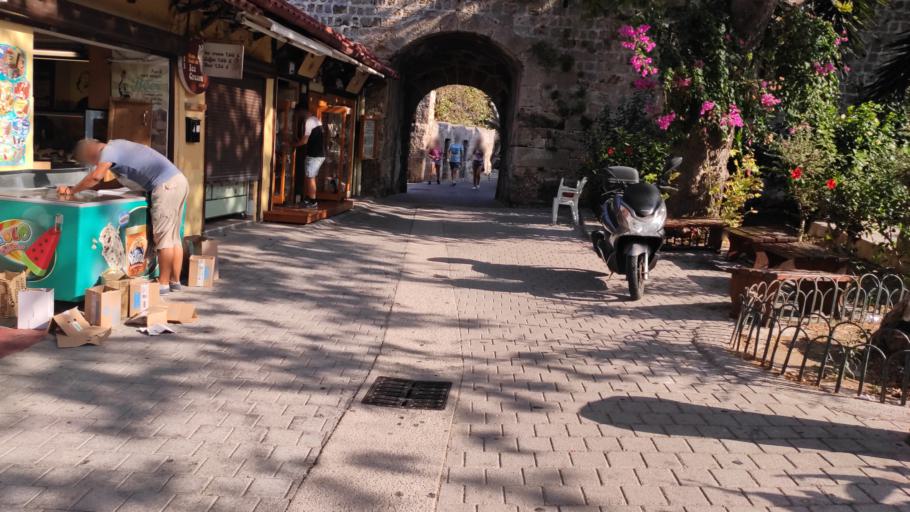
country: GR
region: South Aegean
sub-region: Nomos Dodekanisou
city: Rodos
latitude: 36.4451
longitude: 28.2233
